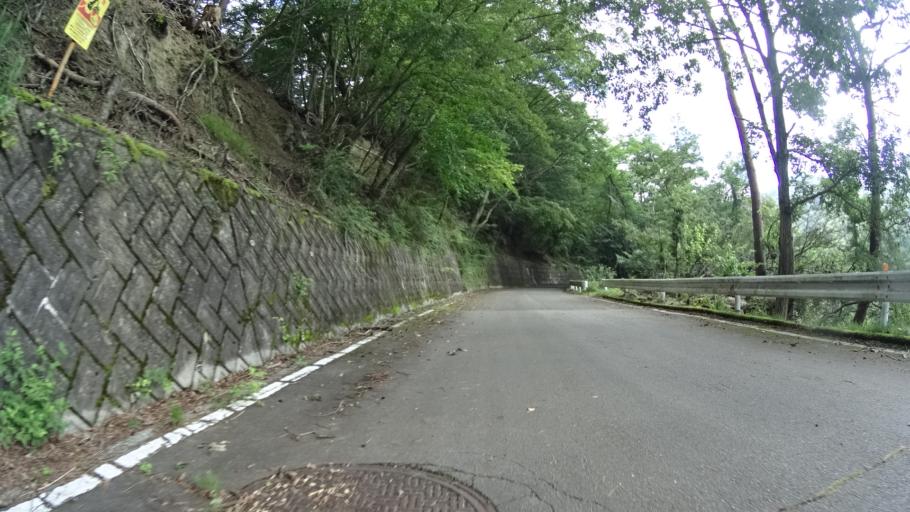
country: JP
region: Yamanashi
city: Enzan
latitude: 35.6194
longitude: 138.7746
